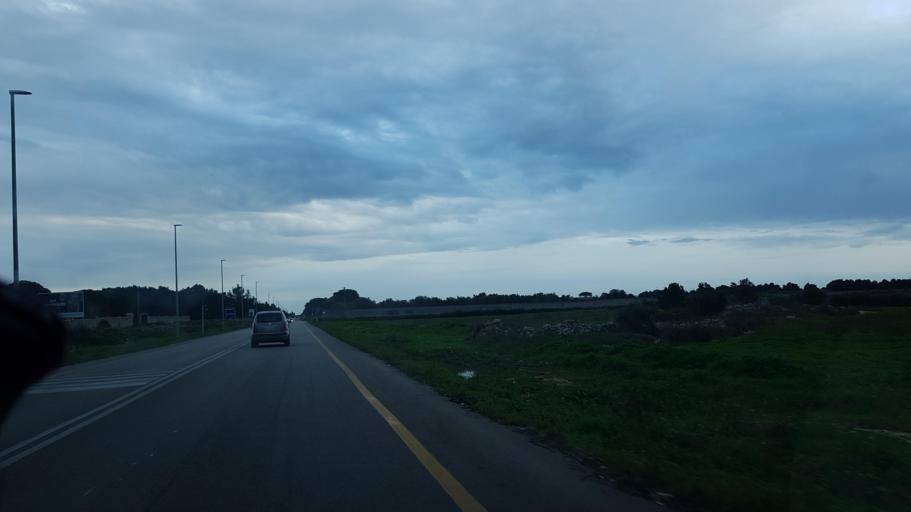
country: IT
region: Apulia
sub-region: Provincia di Lecce
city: Merine
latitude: 40.3435
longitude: 18.2077
